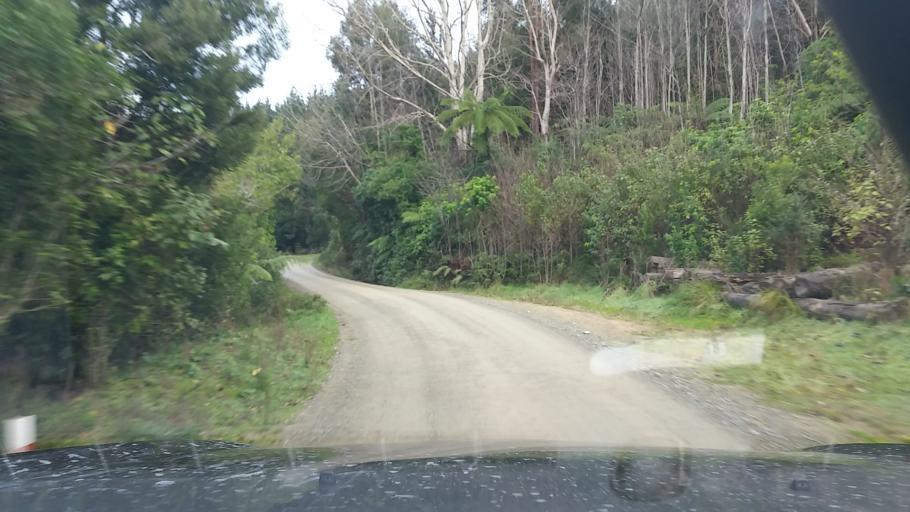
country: NZ
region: Marlborough
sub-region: Marlborough District
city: Picton
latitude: -41.1772
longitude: 174.0728
